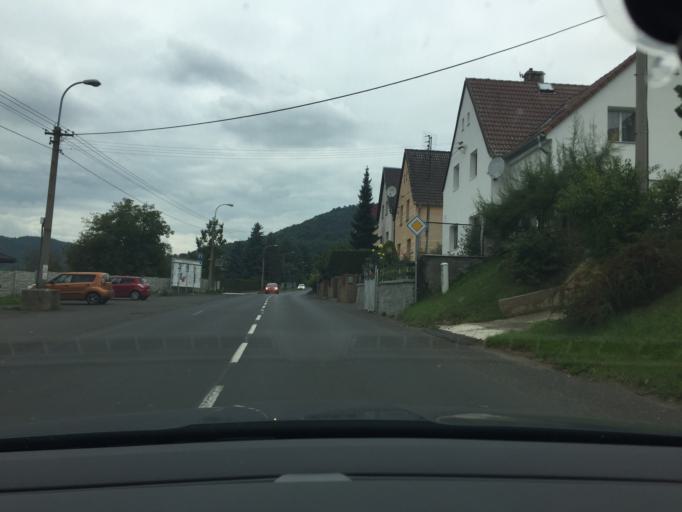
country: CZ
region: Ustecky
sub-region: Okres Usti nad Labem
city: Usti nad Labem
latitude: 50.6230
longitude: 14.0766
